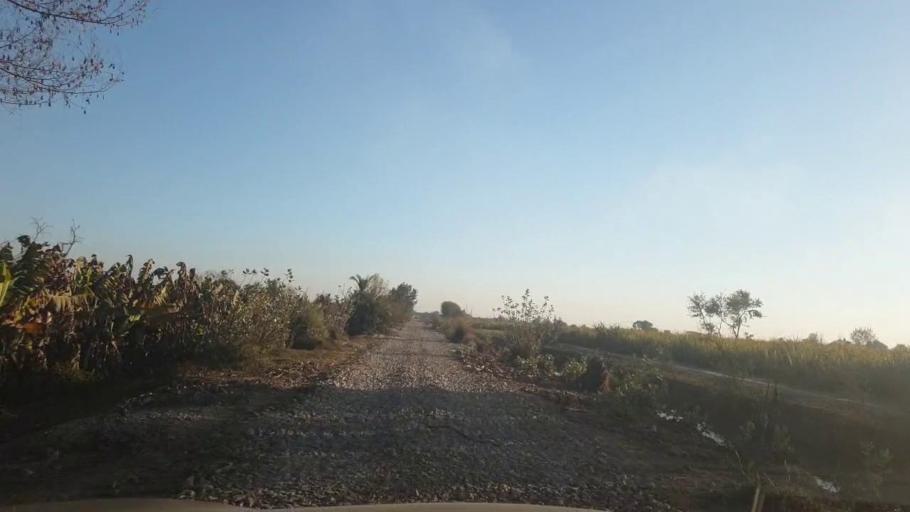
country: PK
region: Sindh
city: Ghotki
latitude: 28.0144
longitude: 69.2681
